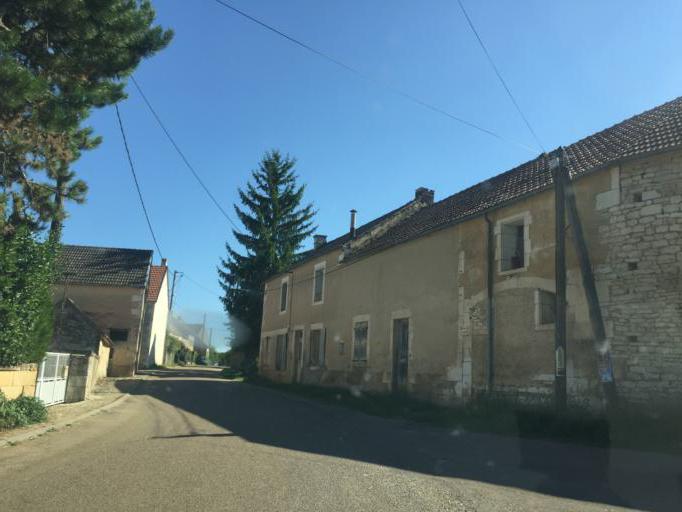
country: FR
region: Bourgogne
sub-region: Departement de l'Yonne
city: Fontenailles
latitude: 47.5438
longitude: 3.3370
